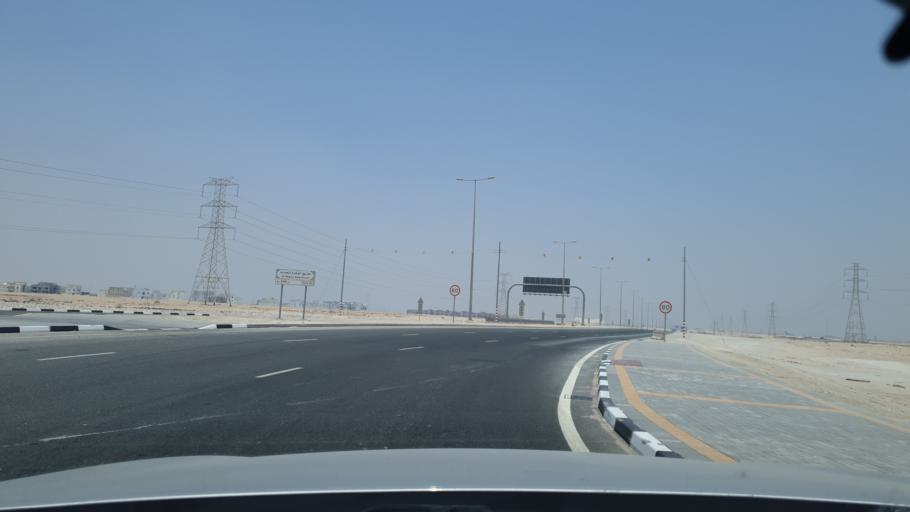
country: QA
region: Al Wakrah
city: Al Wukayr
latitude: 25.1148
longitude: 51.5687
